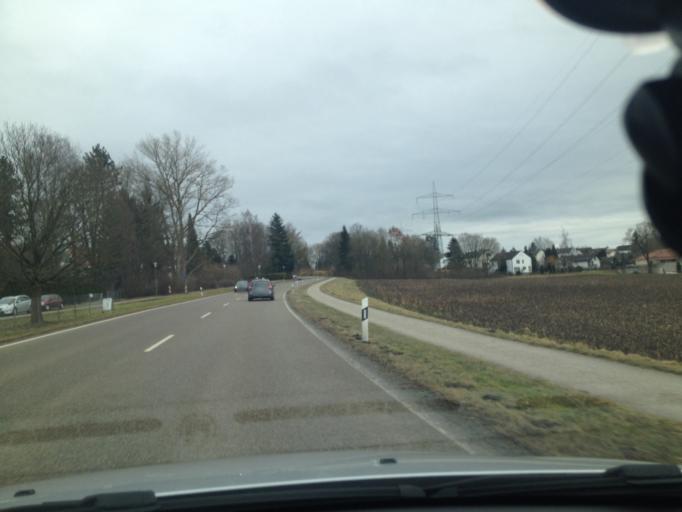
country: DE
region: Bavaria
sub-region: Swabia
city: Aystetten
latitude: 48.4040
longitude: 10.8169
